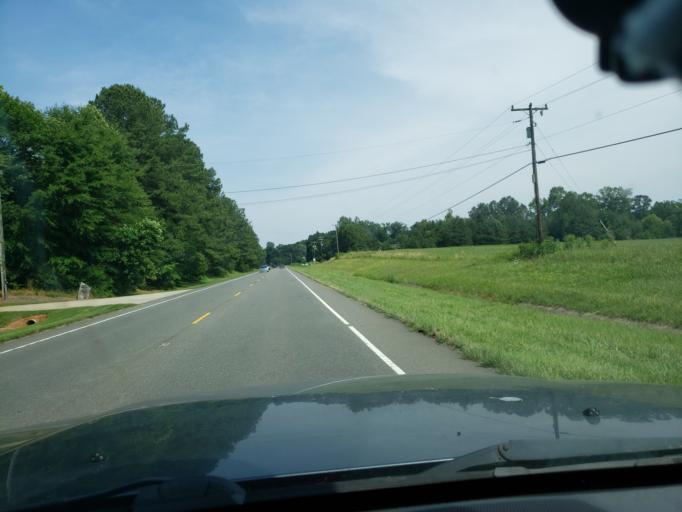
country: US
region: North Carolina
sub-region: Alamance County
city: Saxapahaw
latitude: 35.9349
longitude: -79.2294
